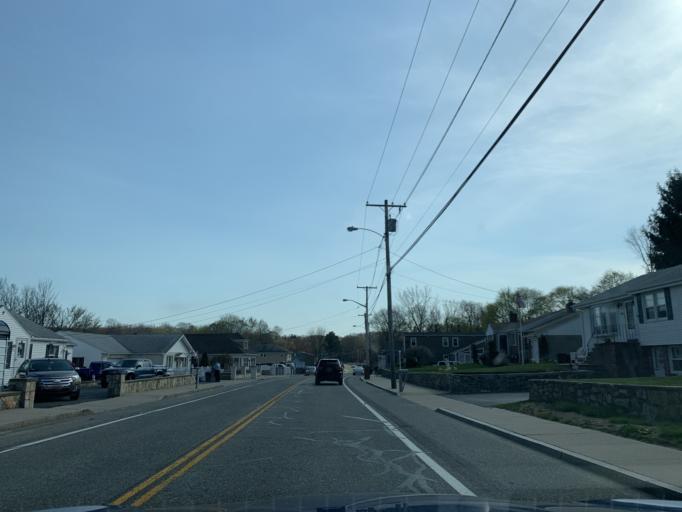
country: US
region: Rhode Island
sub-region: Providence County
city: Johnston
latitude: 41.8008
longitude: -71.5026
